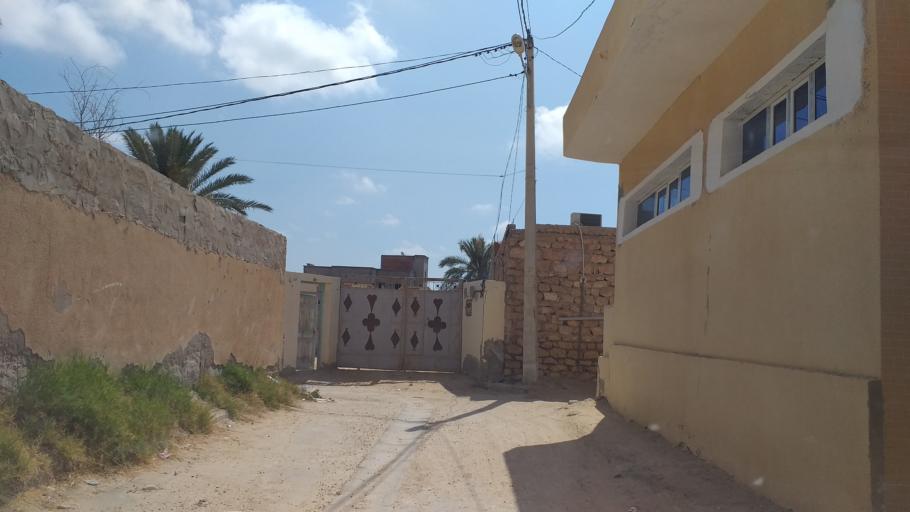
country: TN
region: Qabis
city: Gabes
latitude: 33.9432
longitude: 10.0662
